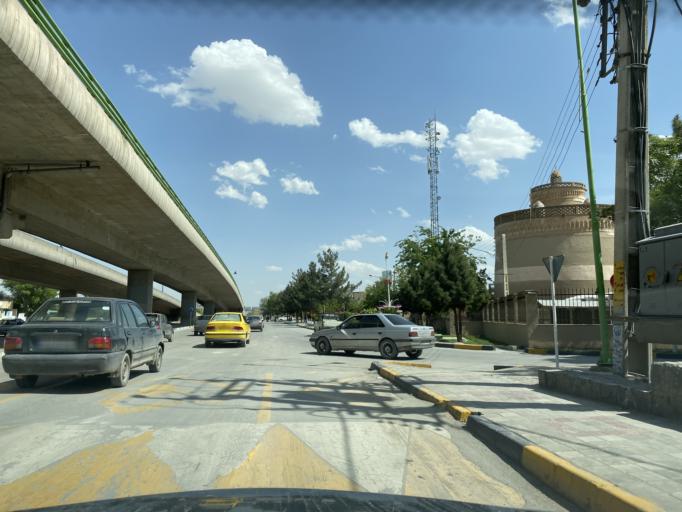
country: IR
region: Isfahan
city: Rehnan
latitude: 32.6855
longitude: 51.6363
